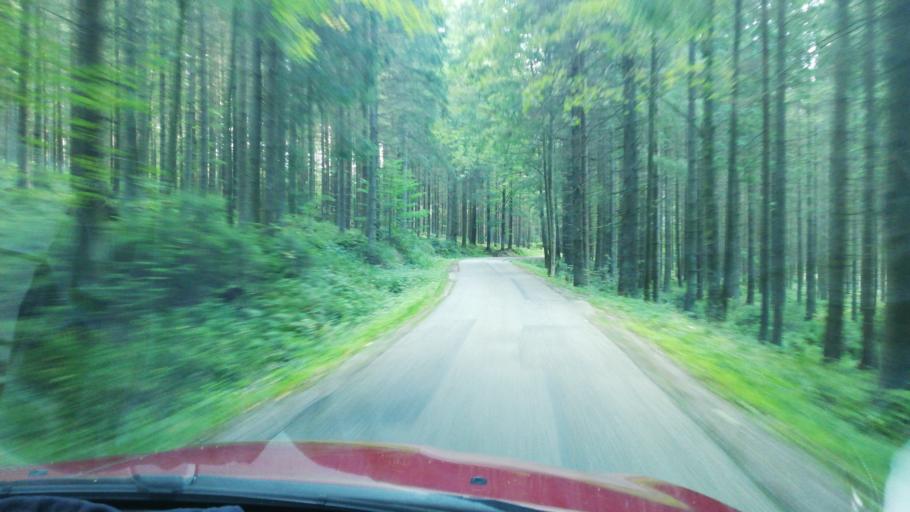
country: AT
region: Lower Austria
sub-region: Politischer Bezirk Zwettl
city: Langschlag
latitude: 48.4843
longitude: 14.8424
